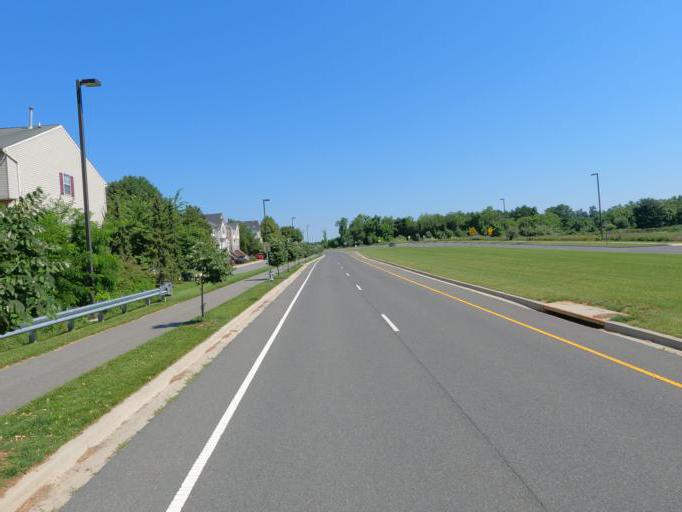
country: US
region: Maryland
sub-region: Montgomery County
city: Germantown
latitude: 39.1967
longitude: -77.2686
